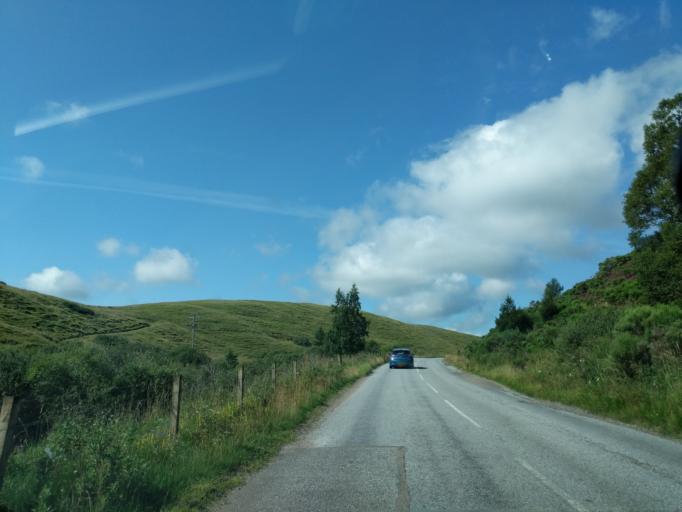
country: GB
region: Scotland
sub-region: Moray
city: Dufftown
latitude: 57.3726
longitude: -3.2399
